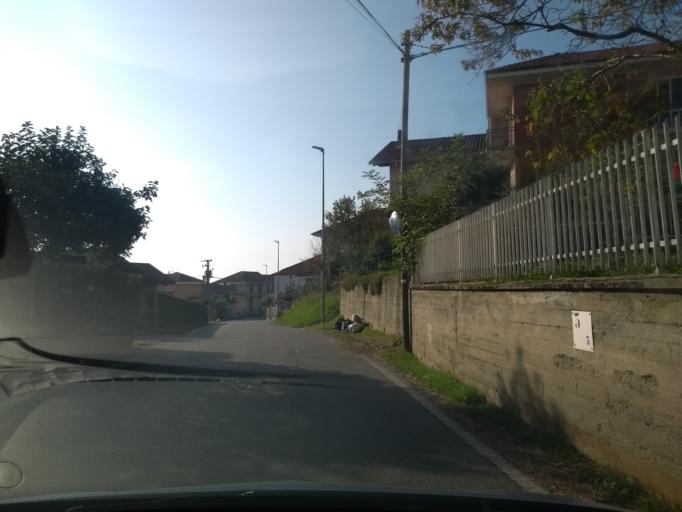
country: IT
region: Piedmont
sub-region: Provincia di Torino
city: Vallo Torinese
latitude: 45.2258
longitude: 7.4970
